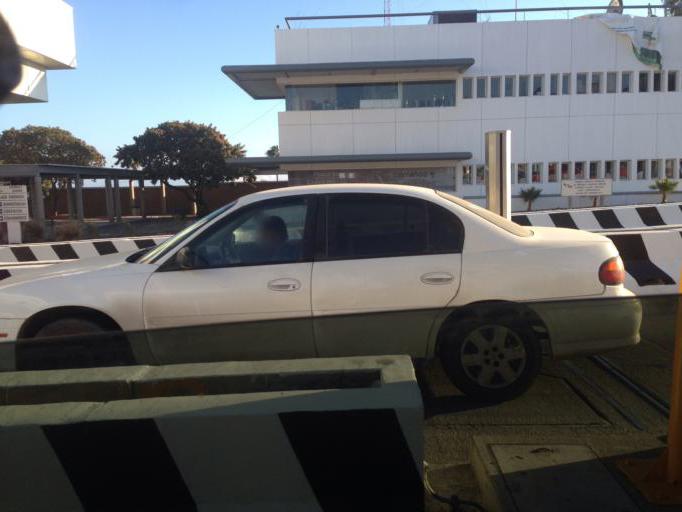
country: MX
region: Baja California
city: El Sauzal
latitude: 31.9030
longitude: -116.7329
